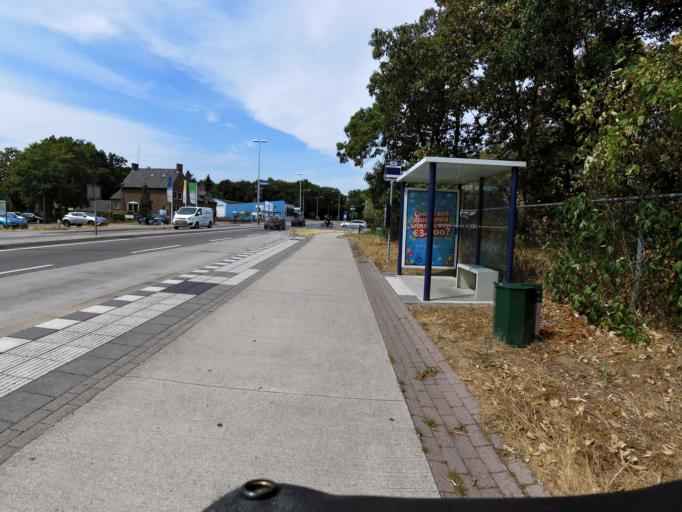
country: NL
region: Limburg
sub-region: Gemeente Bergen
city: Wellerlooi
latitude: 51.5574
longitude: 6.0942
